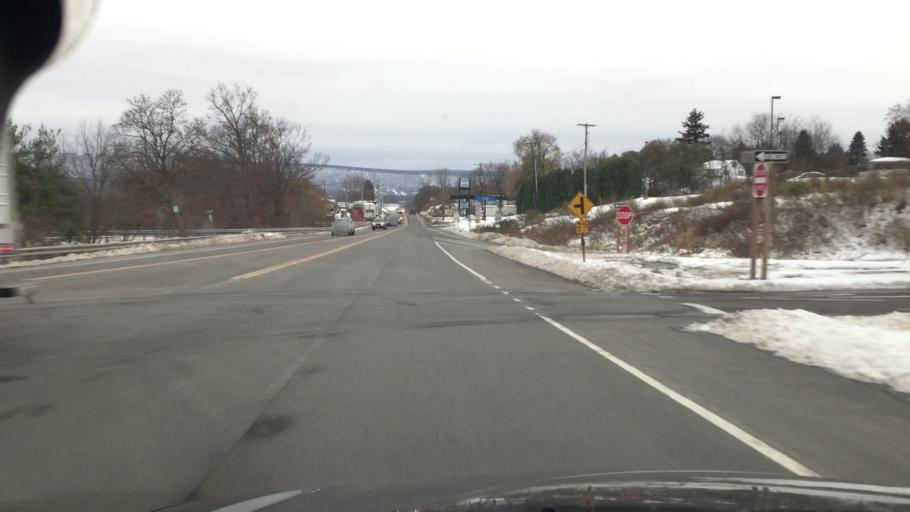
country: US
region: Pennsylvania
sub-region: Luzerne County
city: Conyngham
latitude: 41.0246
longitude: -76.0791
